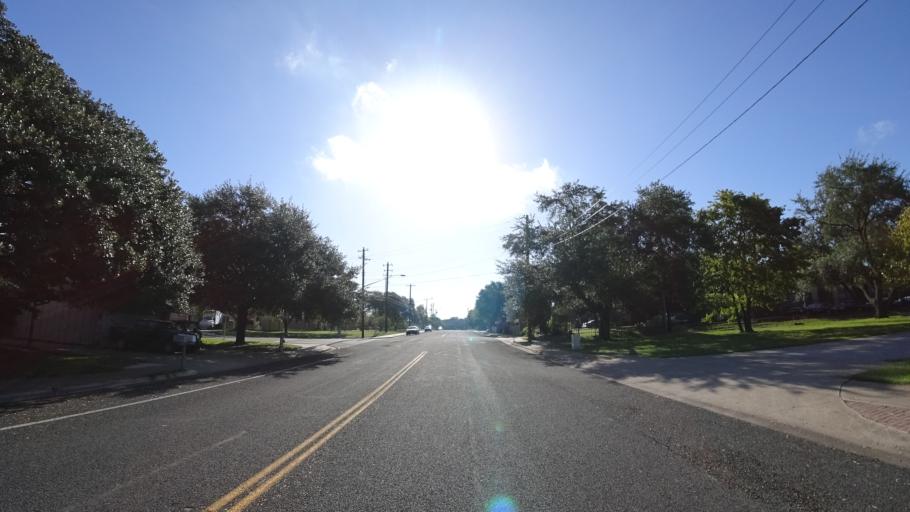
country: US
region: Texas
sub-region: Travis County
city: Rollingwood
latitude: 30.2101
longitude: -97.8076
